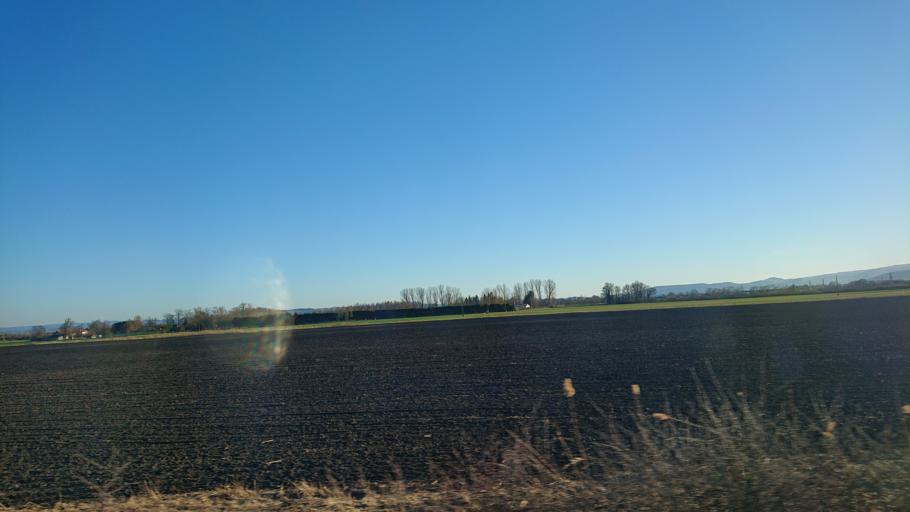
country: FR
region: Auvergne
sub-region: Departement du Puy-de-Dome
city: Riom
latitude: 45.9041
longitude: 3.1649
